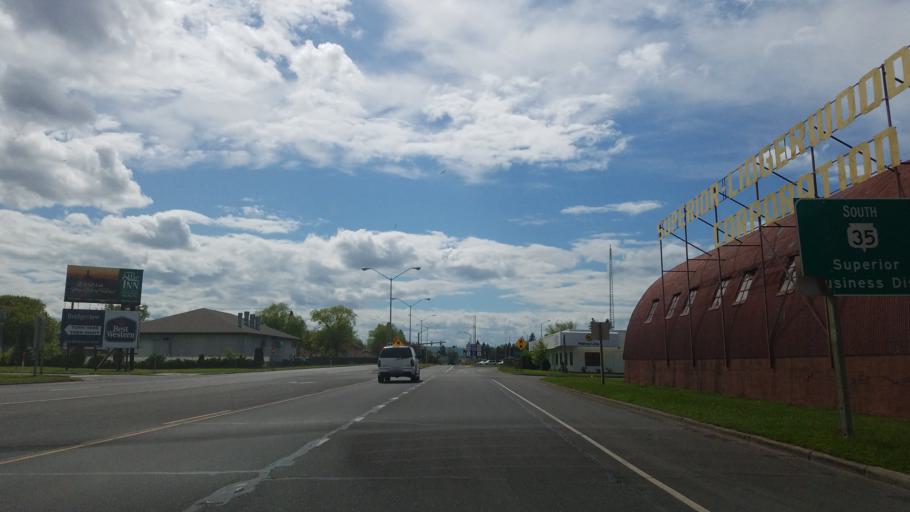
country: US
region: Wisconsin
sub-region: Douglas County
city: Superior
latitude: 46.7339
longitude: -92.0923
